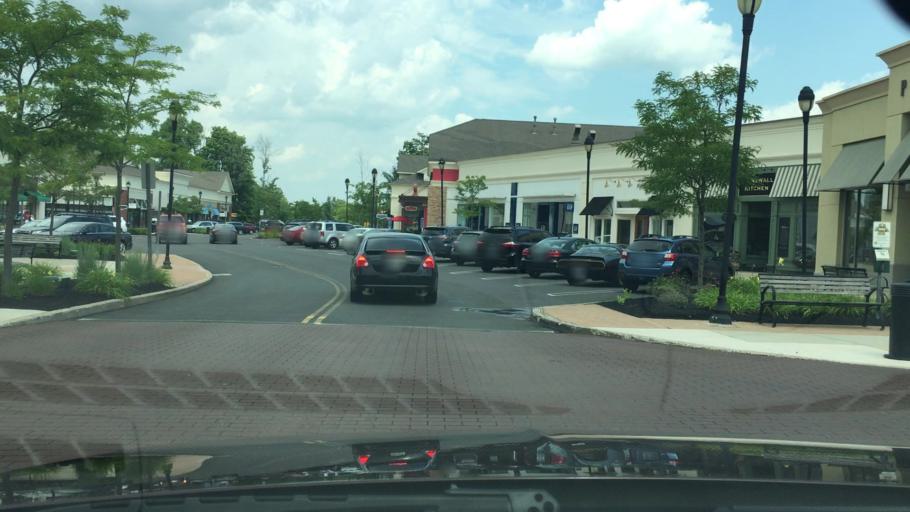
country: US
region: Connecticut
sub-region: Hartford County
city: Manchester
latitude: 41.8121
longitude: -72.5562
